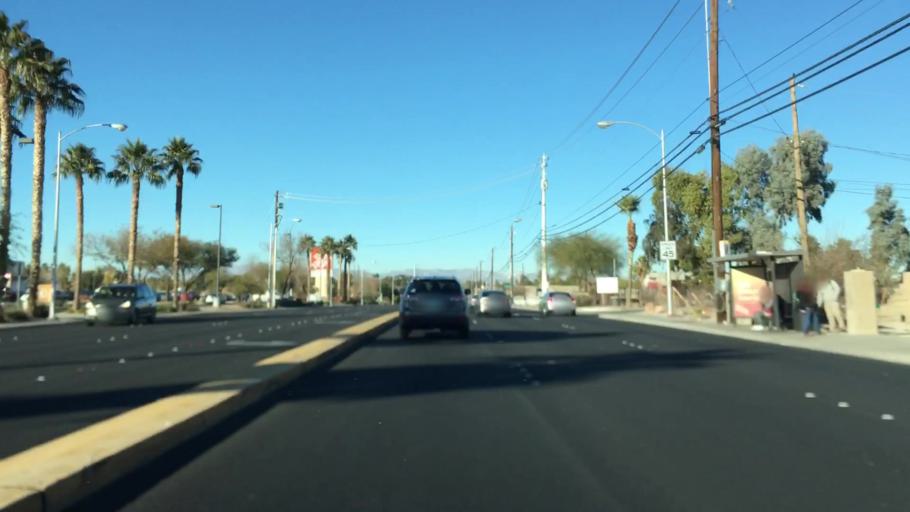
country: US
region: Nevada
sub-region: Clark County
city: Whitney
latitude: 36.0794
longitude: -115.1009
